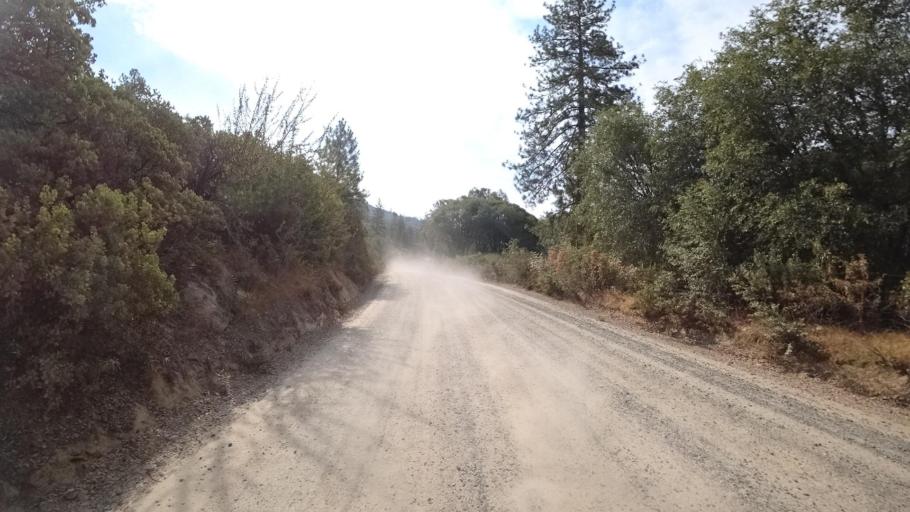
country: US
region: California
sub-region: Mariposa County
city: Midpines
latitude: 37.4968
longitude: -119.7973
